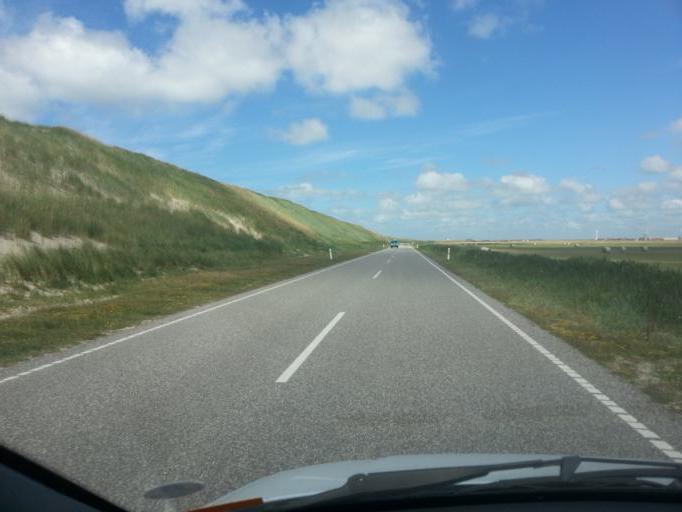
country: DK
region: Central Jutland
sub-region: Lemvig Kommune
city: Harboore
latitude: 56.4436
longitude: 8.1251
